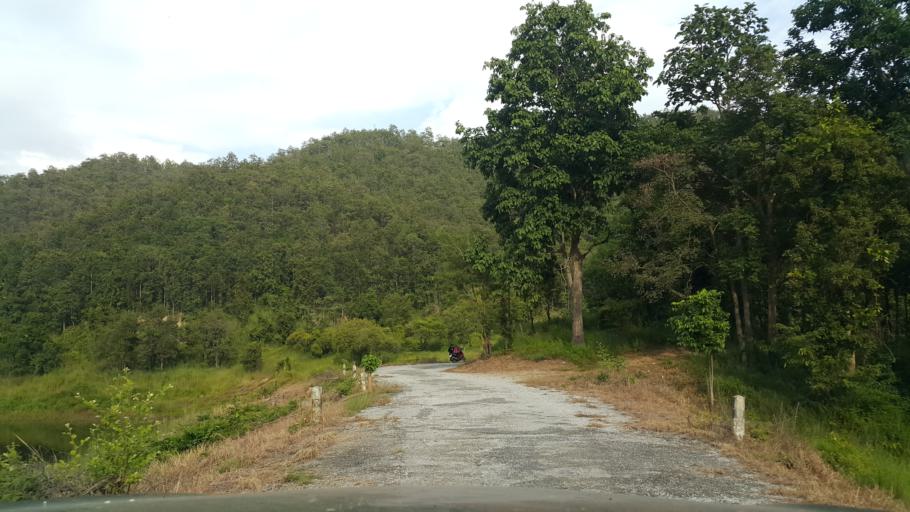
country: TH
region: Chiang Mai
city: San Sai
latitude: 18.9279
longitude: 99.0831
